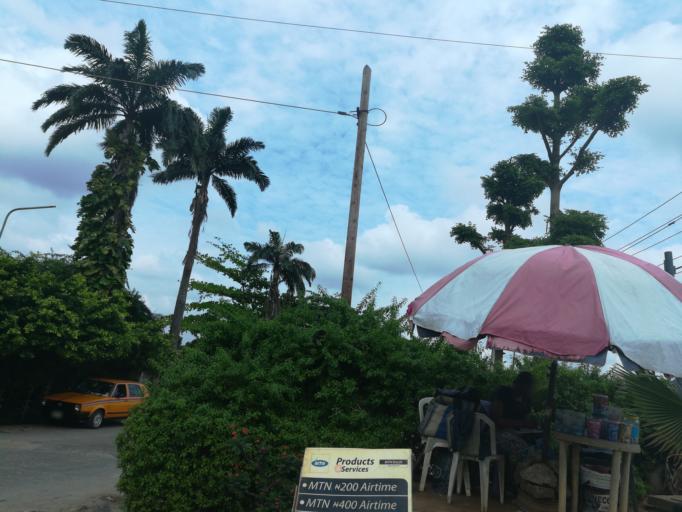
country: NG
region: Lagos
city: Somolu
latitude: 6.5475
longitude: 3.3818
